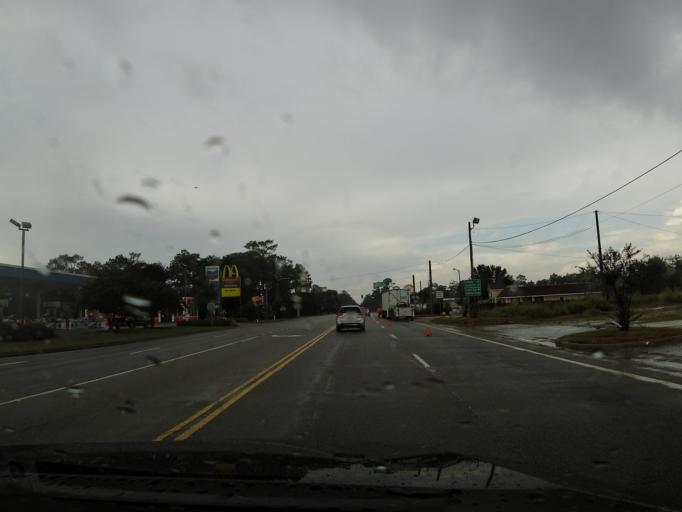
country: US
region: Georgia
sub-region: Wayne County
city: Jesup
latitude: 31.5949
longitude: -81.8704
